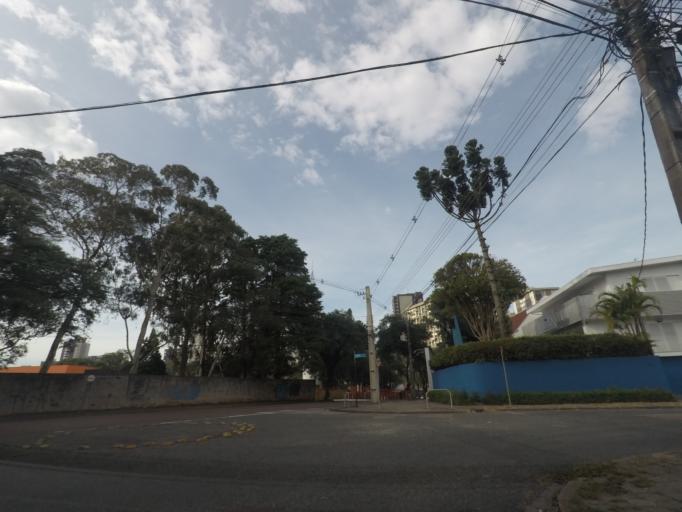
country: BR
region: Parana
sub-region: Curitiba
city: Curitiba
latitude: -25.4277
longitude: -49.2944
